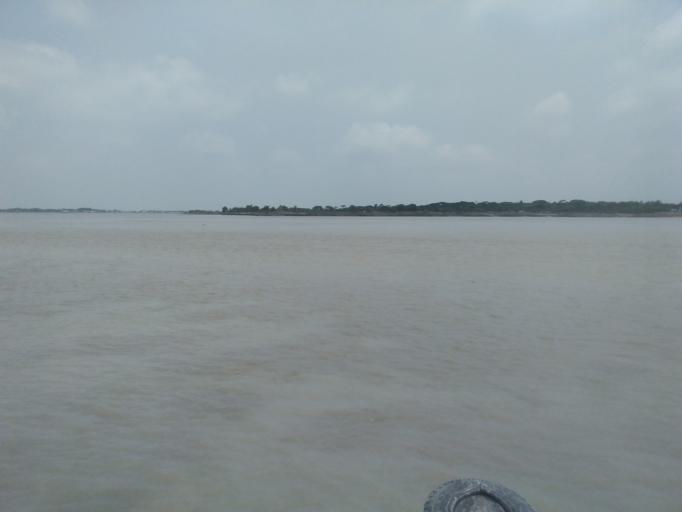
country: BD
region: Khulna
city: Phultala
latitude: 22.6422
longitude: 89.4132
